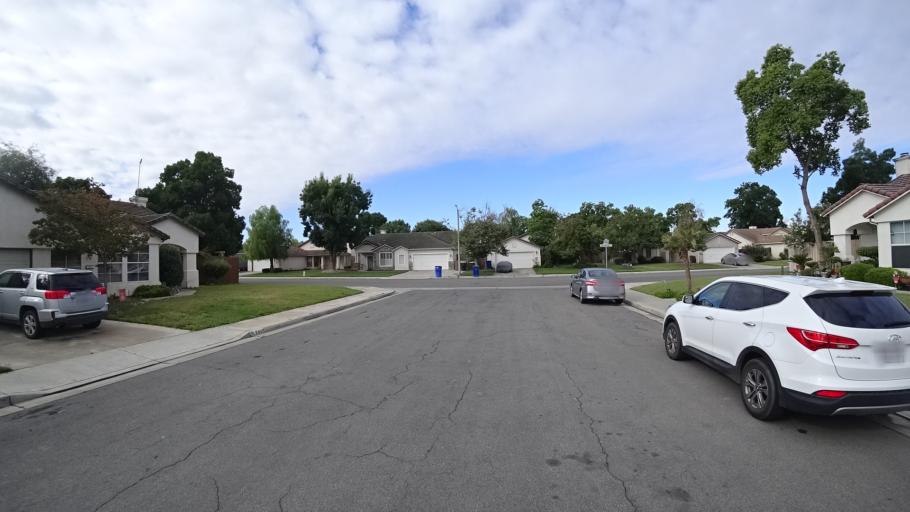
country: US
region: California
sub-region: Kings County
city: Lucerne
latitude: 36.3636
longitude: -119.6335
